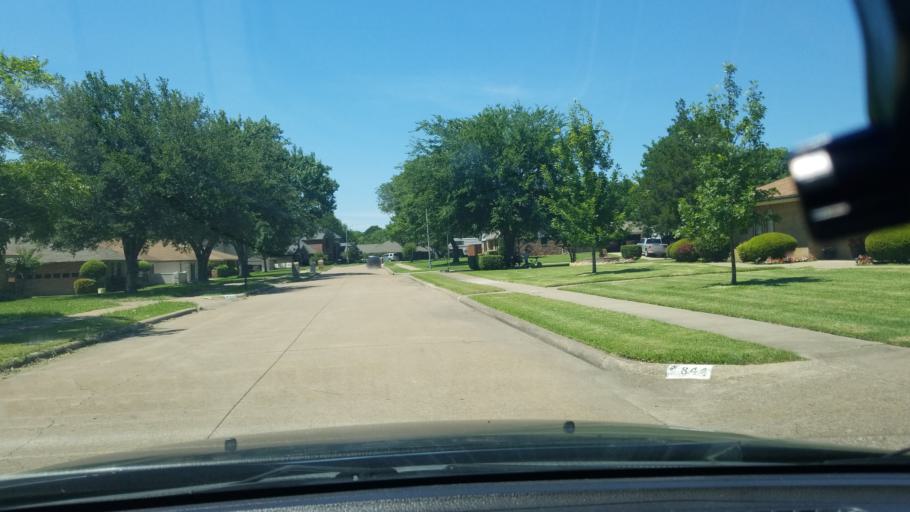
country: US
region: Texas
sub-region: Dallas County
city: Mesquite
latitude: 32.7579
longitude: -96.6031
